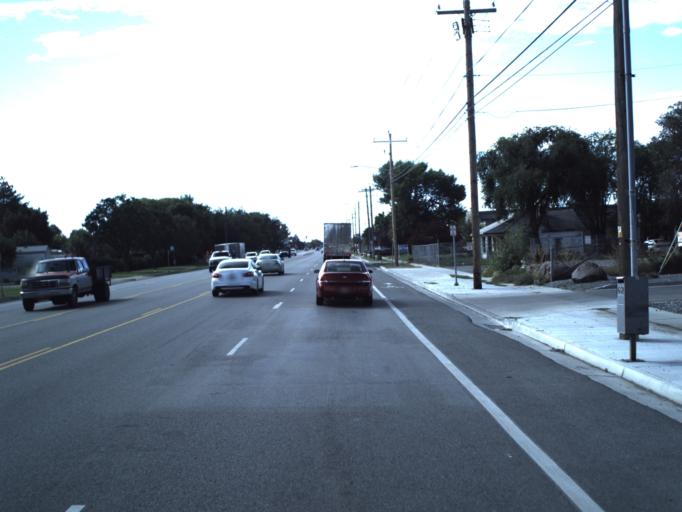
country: US
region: Utah
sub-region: Salt Lake County
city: Salt Lake City
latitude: 40.7548
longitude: -111.9391
